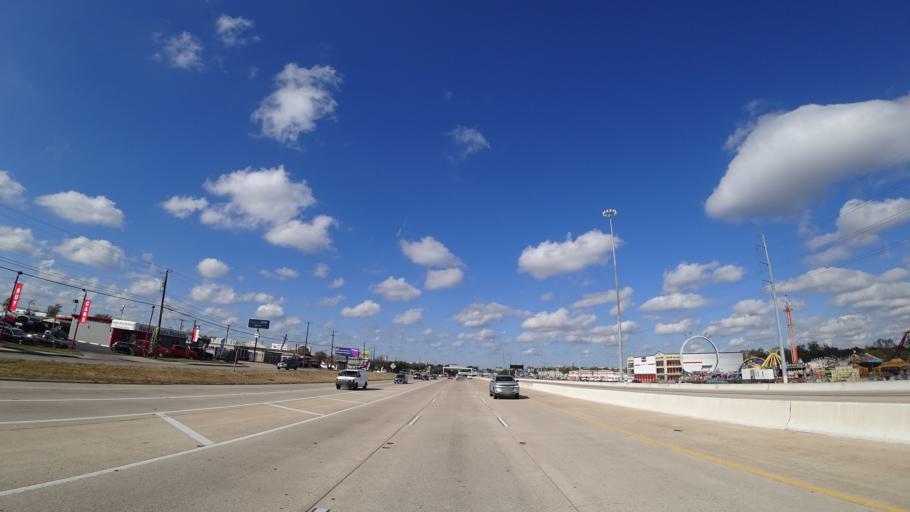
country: US
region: Texas
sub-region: Travis County
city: Austin
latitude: 30.2199
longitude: -97.7585
